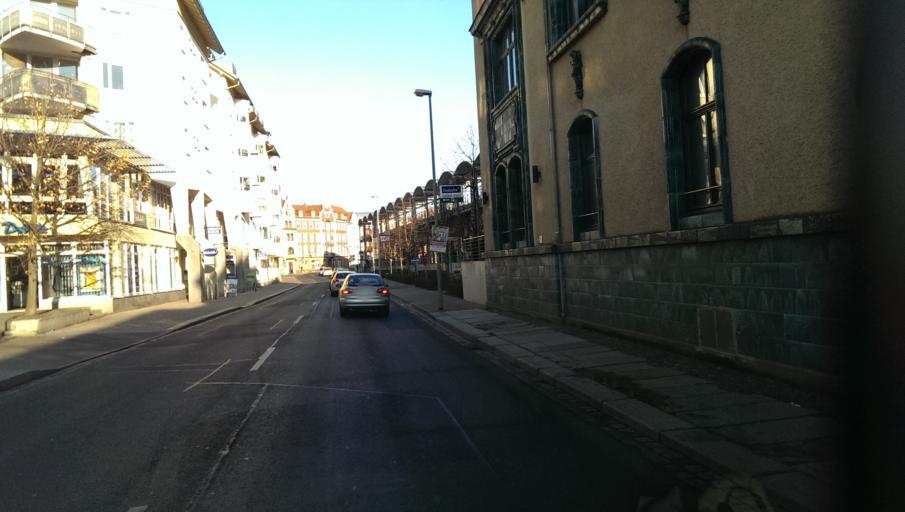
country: DE
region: Saxony
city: Meissen
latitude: 51.1596
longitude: 13.4722
